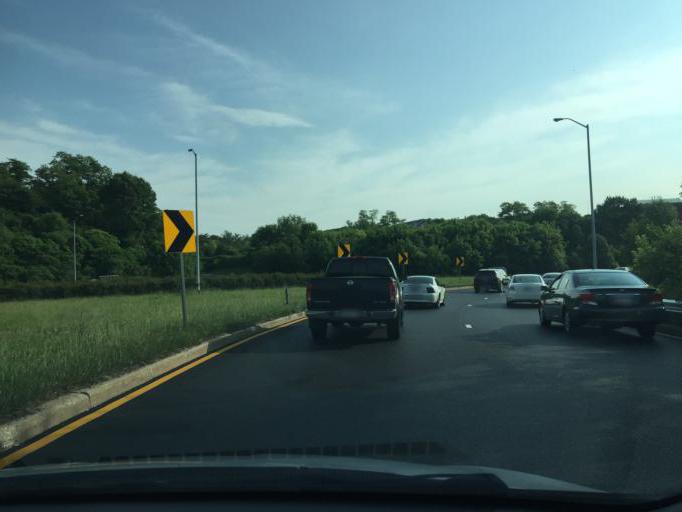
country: US
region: Maryland
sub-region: Baltimore County
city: Hunt Valley
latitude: 39.4945
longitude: -76.6658
